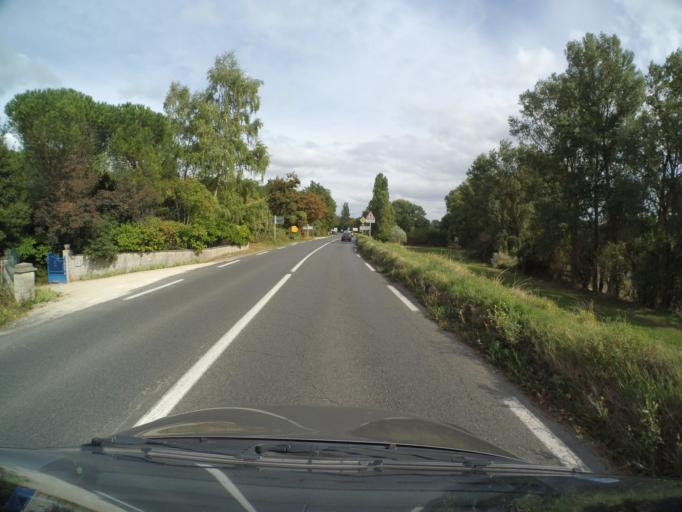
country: FR
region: Centre
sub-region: Departement d'Indre-et-Loire
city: Saint-Pierre-des-Corps
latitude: 47.4047
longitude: 0.7310
